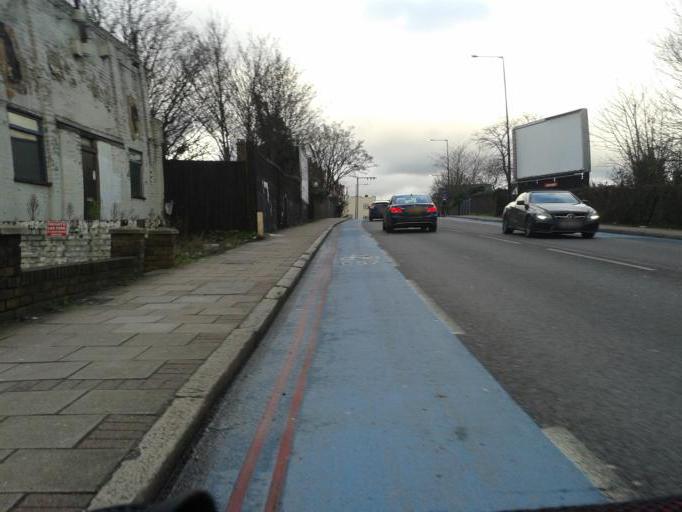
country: GB
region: England
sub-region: Greater London
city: Mitcham
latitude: 51.4224
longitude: -0.1741
